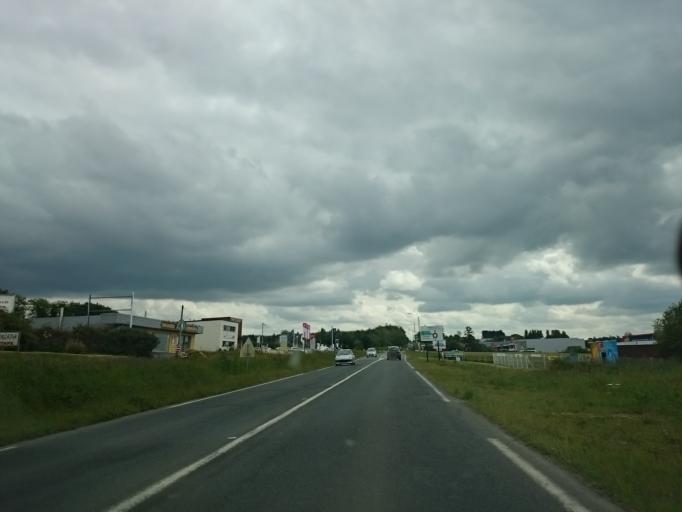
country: FR
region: Brittany
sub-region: Departement des Cotes-d'Armor
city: Saint-Quay-Perros
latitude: 48.7692
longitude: -3.4471
